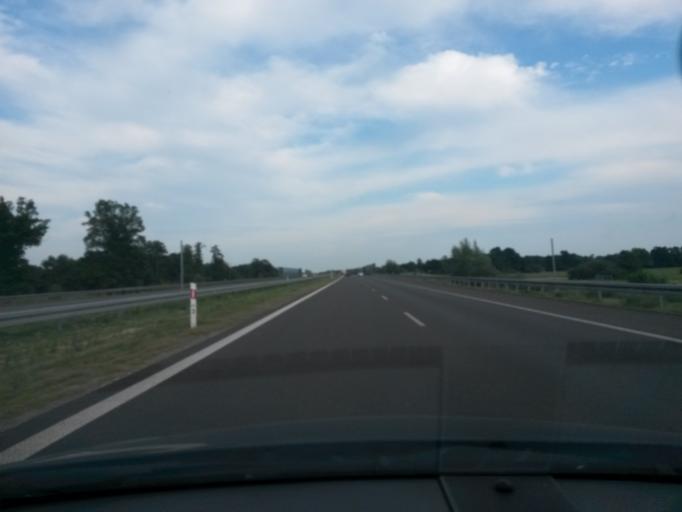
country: PL
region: Greater Poland Voivodeship
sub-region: Powiat turecki
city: Brudzew
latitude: 52.1258
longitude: 18.6740
